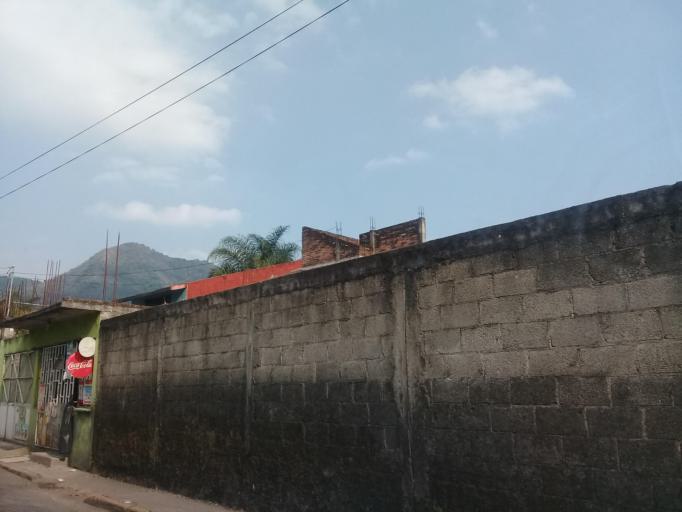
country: MX
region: Veracruz
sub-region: Ixhuatlancillo
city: Union y Progreso
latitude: 18.8671
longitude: -97.1049
